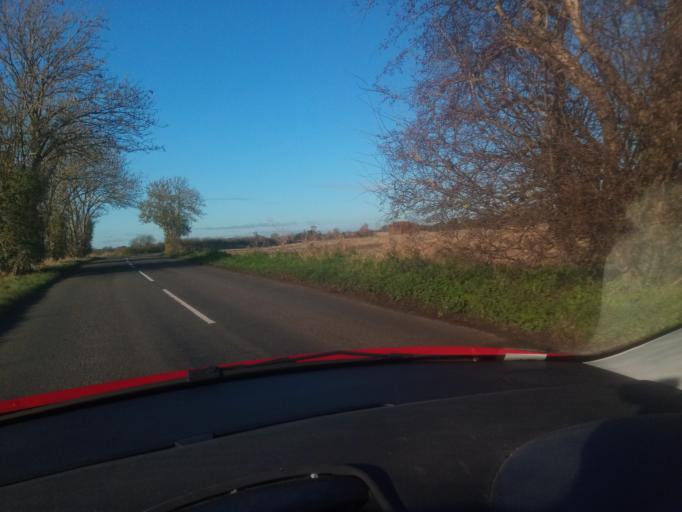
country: GB
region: England
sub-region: Derbyshire
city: Melbourne
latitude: 52.8523
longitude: -1.4320
